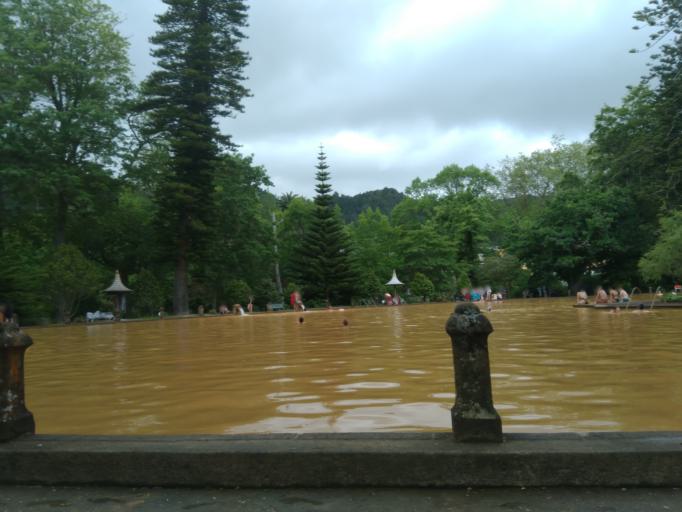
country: PT
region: Azores
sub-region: Povoacao
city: Furnas
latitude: 37.7714
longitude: -25.3150
